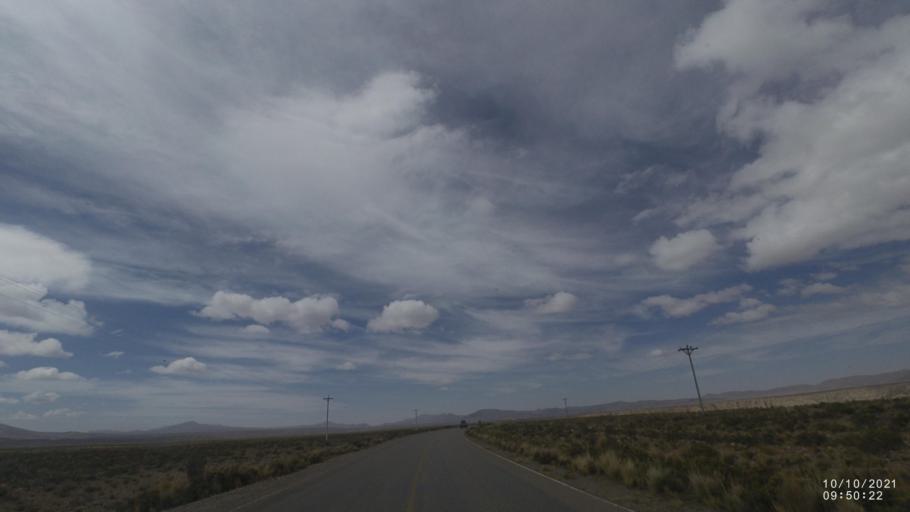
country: BO
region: La Paz
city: Colquiri
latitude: -17.2420
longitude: -67.3333
